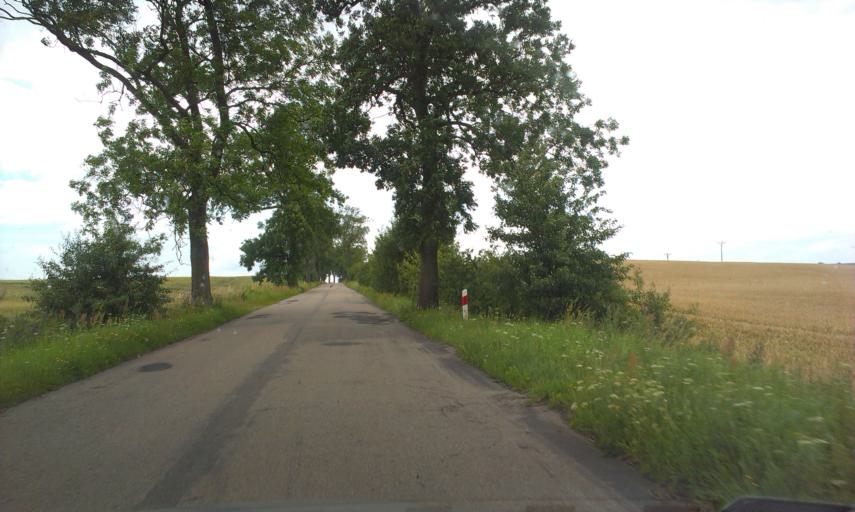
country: PL
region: West Pomeranian Voivodeship
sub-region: Powiat szczecinecki
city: Barwice
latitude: 53.7221
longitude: 16.3546
